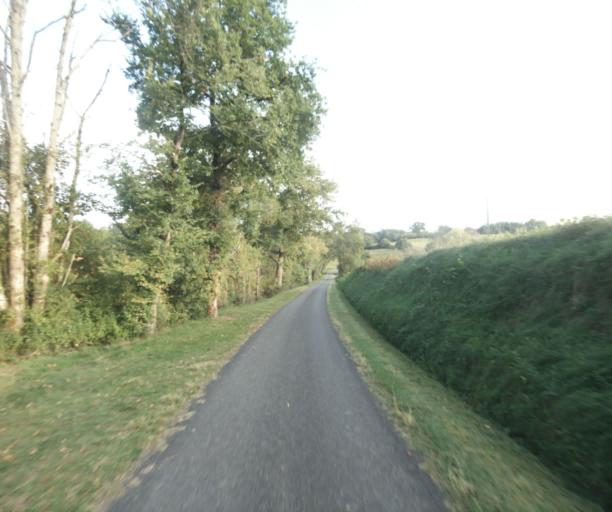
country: FR
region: Midi-Pyrenees
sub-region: Departement du Gers
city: Le Houga
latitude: 43.8468
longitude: -0.1255
